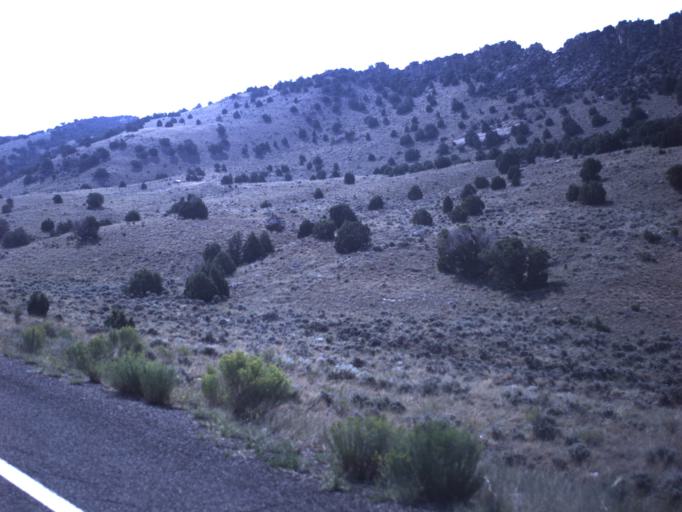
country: US
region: Utah
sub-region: Daggett County
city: Manila
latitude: 40.9311
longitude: -109.7079
